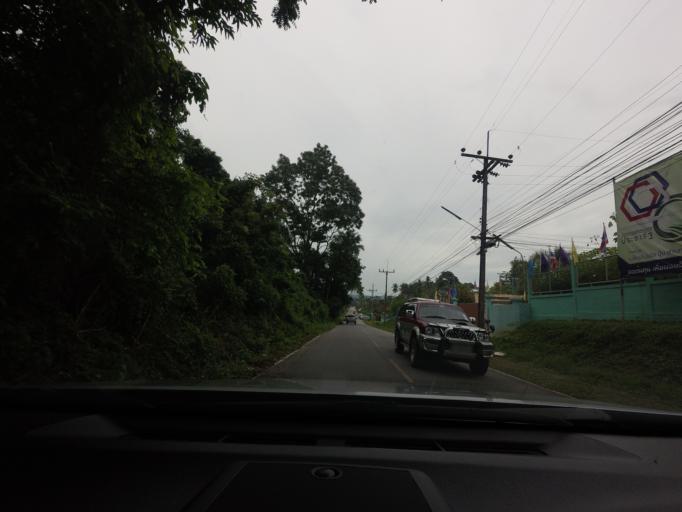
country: TH
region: Narathiwat
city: Rueso
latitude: 6.4022
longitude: 101.5249
